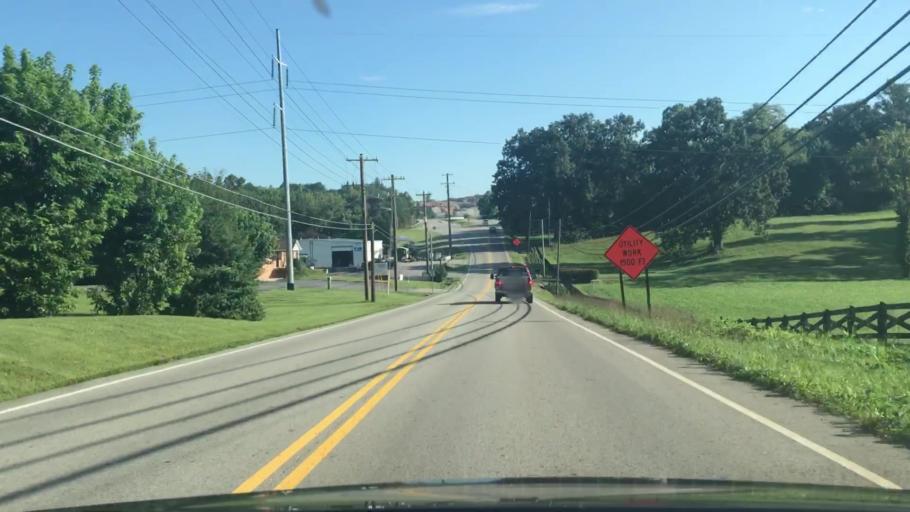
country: US
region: Tennessee
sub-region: Overton County
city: Livingston
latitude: 36.3918
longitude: -85.3034
